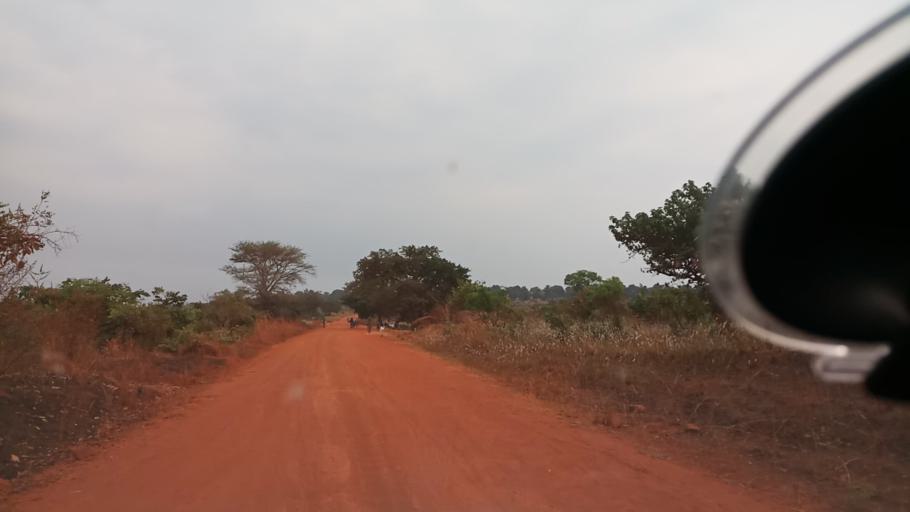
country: ZM
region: Luapula
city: Nchelenge
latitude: -9.1079
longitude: 28.3023
